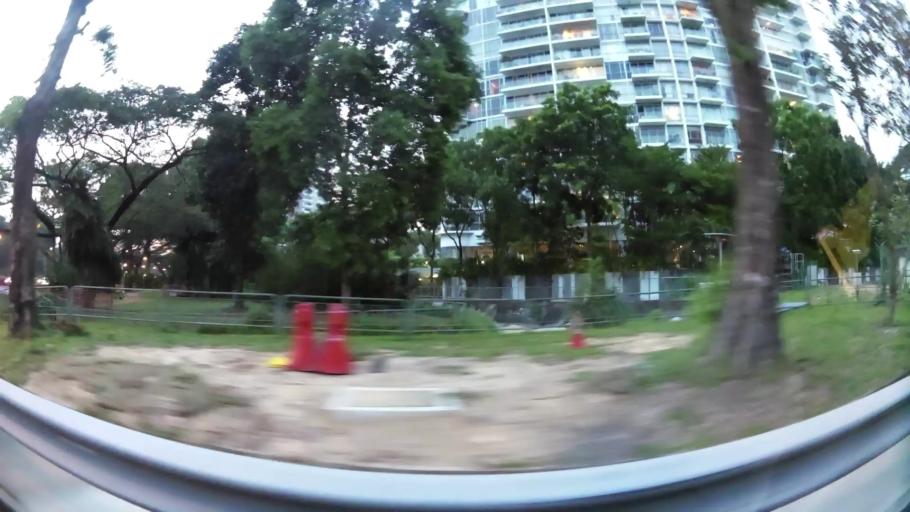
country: SG
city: Singapore
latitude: 1.2979
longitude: 103.8980
